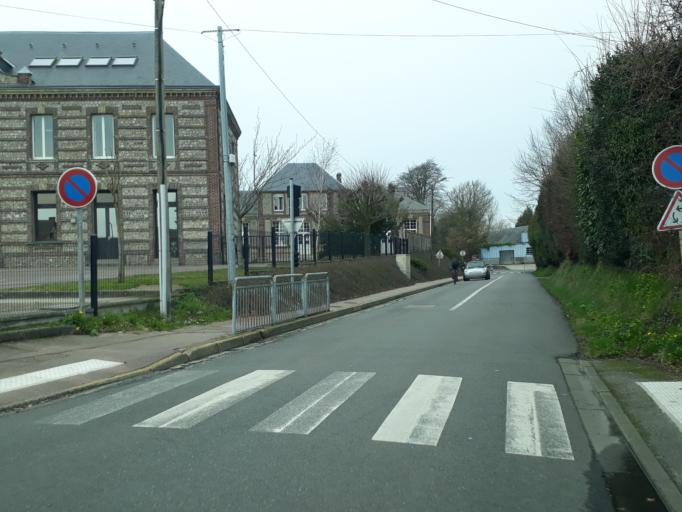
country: FR
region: Haute-Normandie
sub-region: Departement de la Seine-Maritime
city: Goderville
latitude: 49.6450
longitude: 0.3643
